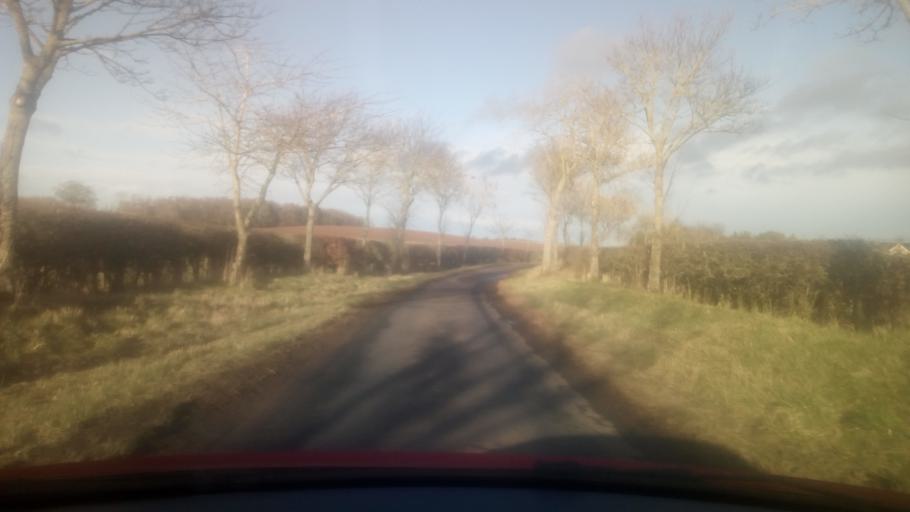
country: GB
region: Scotland
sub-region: The Scottish Borders
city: Duns
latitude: 55.7369
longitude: -2.3348
